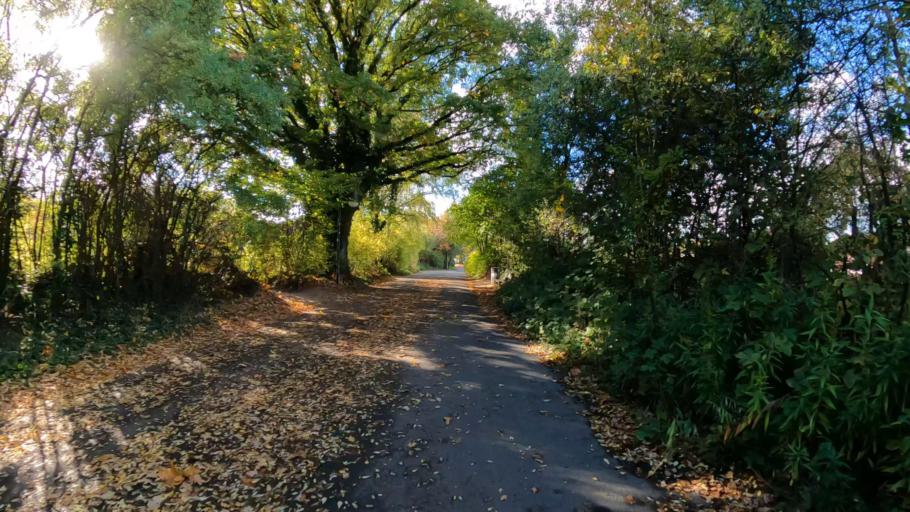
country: DE
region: Schleswig-Holstein
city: Ahrensburg
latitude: 53.6803
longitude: 10.2333
